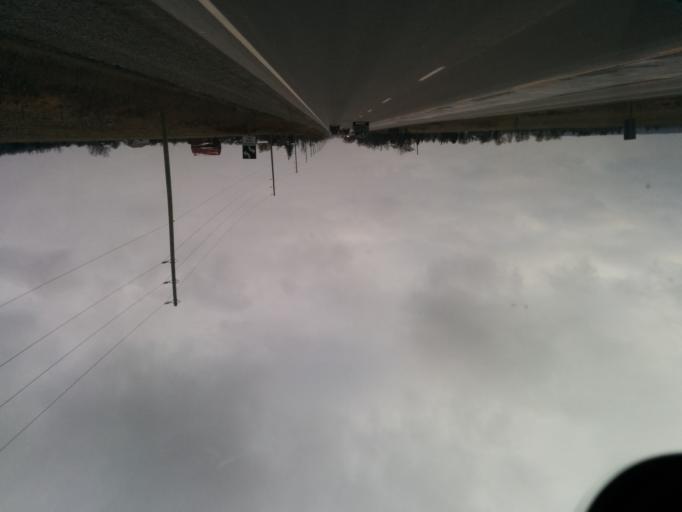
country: CA
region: Ontario
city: Brampton
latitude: 43.7591
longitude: -79.8589
